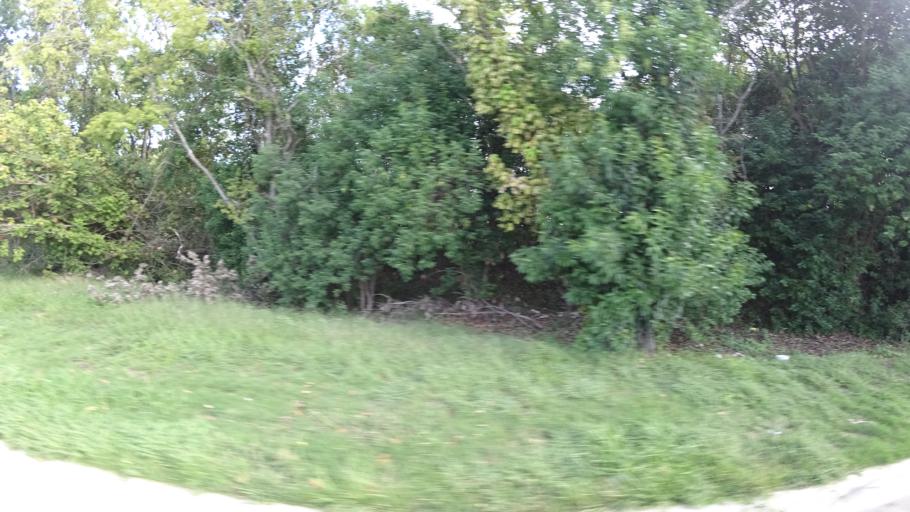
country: US
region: Texas
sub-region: Travis County
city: Austin
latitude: 30.2066
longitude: -97.7398
